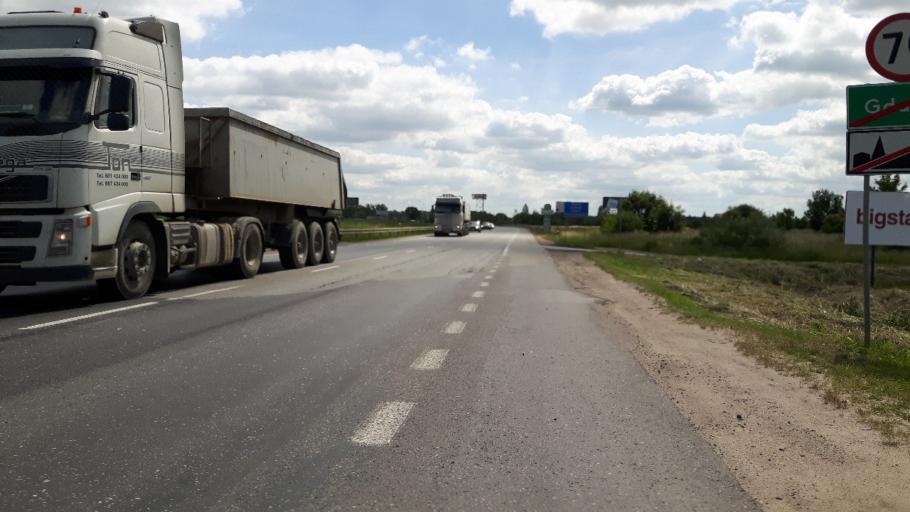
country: PL
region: Pomeranian Voivodeship
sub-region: Gdansk
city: Gdansk
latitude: 54.3415
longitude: 18.7272
